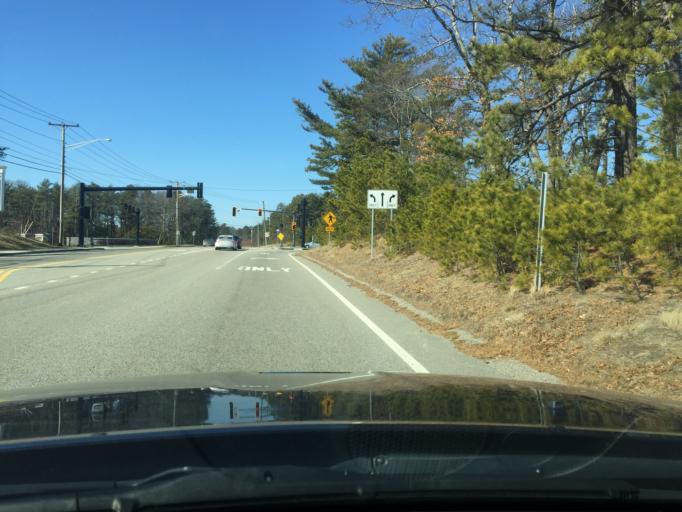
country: US
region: Massachusetts
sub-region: Plymouth County
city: North Plymouth
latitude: 41.9465
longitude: -70.7151
